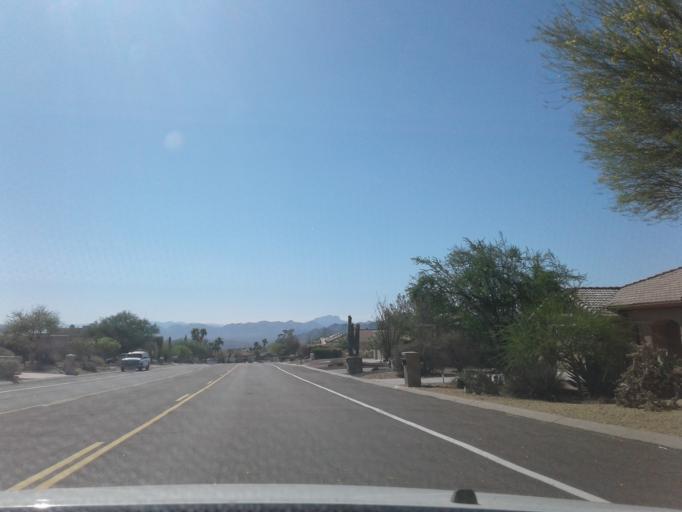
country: US
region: Arizona
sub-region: Maricopa County
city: Fountain Hills
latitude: 33.5948
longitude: -111.7542
